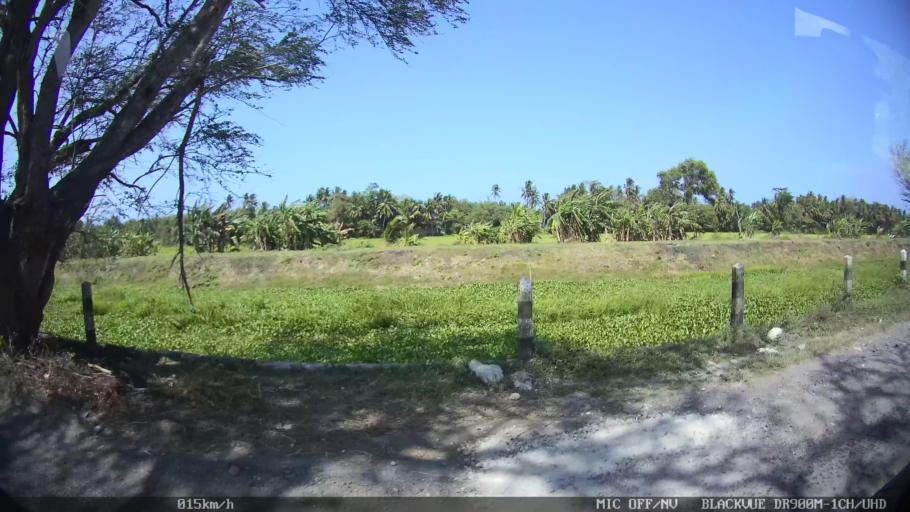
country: ID
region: Daerah Istimewa Yogyakarta
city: Srandakan
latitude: -7.9454
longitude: 110.1749
